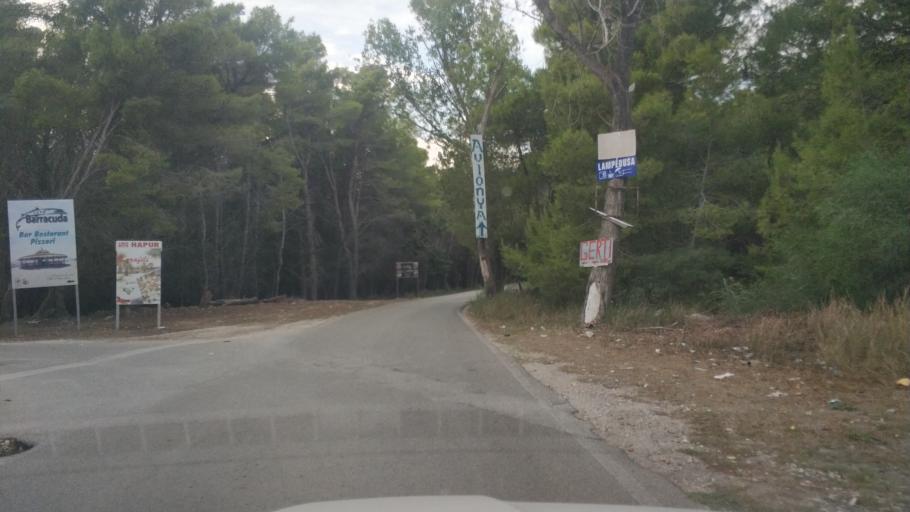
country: AL
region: Vlore
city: Vlore
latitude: 40.4919
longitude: 19.4366
